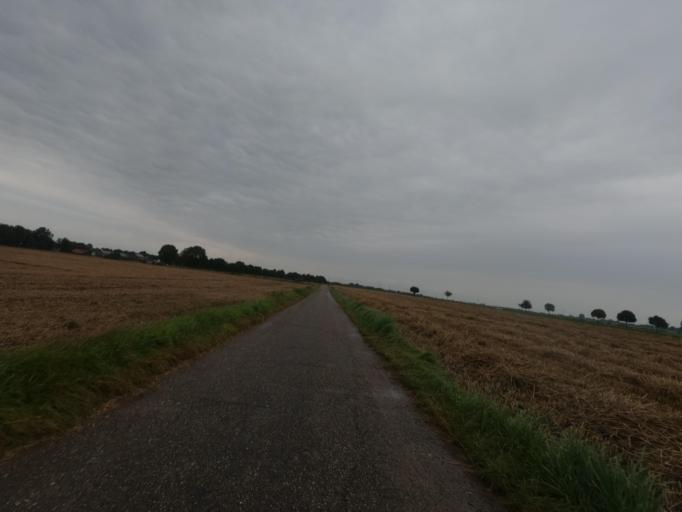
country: DE
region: North Rhine-Westphalia
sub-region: Regierungsbezirk Koln
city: Ubach-Palenberg
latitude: 50.9389
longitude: 6.1550
